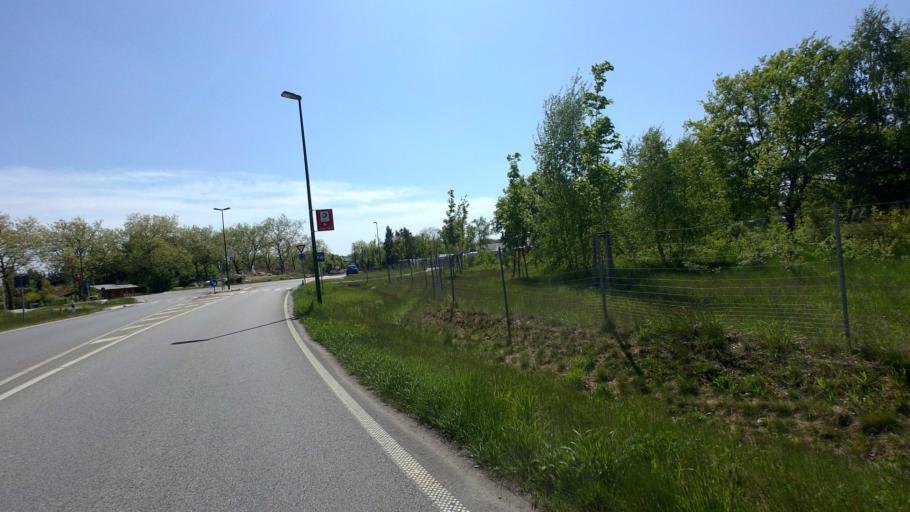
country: DE
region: Brandenburg
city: Konigs Wusterhausen
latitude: 52.2761
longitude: 13.6310
